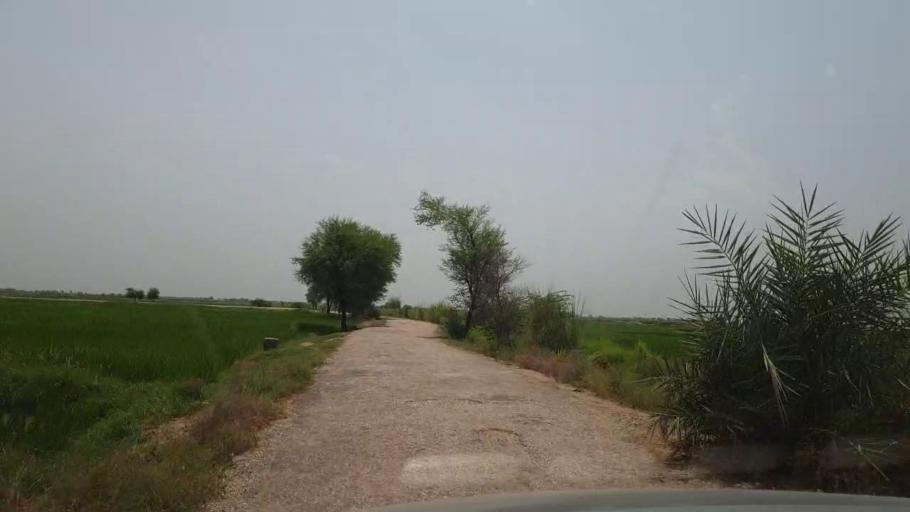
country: PK
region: Sindh
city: Garhi Yasin
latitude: 27.8712
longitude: 68.5011
